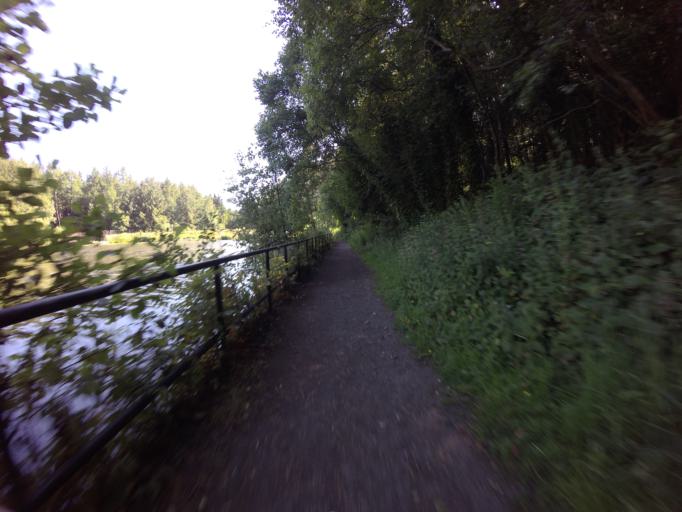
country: GB
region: Scotland
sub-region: West Lothian
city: Livingston
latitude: 55.8936
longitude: -3.5511
